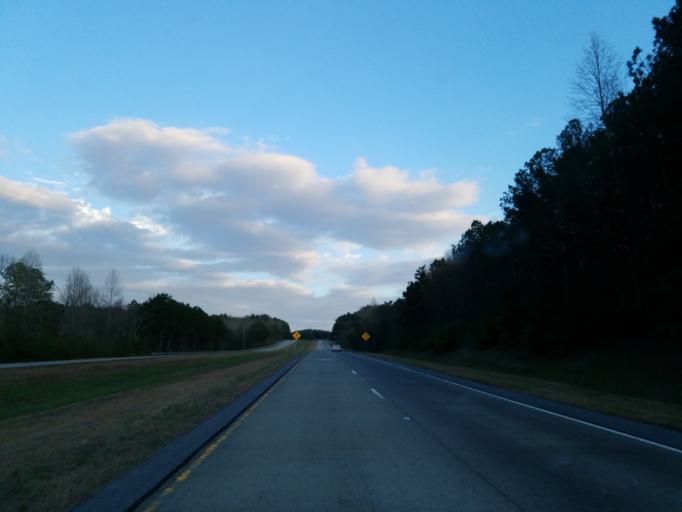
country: US
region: Georgia
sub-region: Pickens County
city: Nelson
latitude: 34.3757
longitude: -84.3838
